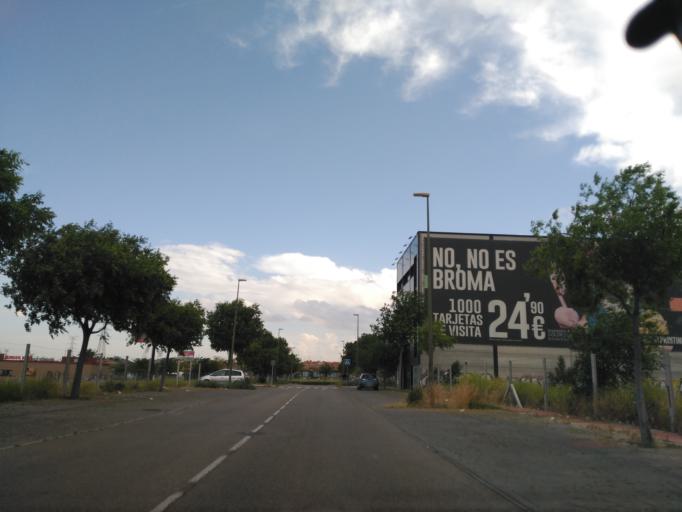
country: ES
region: Madrid
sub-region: Provincia de Madrid
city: Villaverde
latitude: 40.3327
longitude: -3.7169
